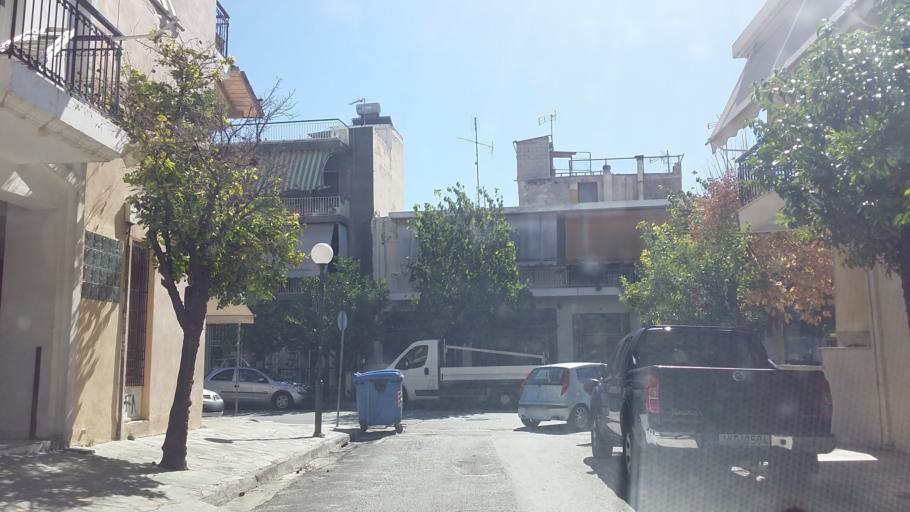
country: GR
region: Attica
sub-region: Nomarchia Athinas
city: Ilion
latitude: 38.0295
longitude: 23.6894
